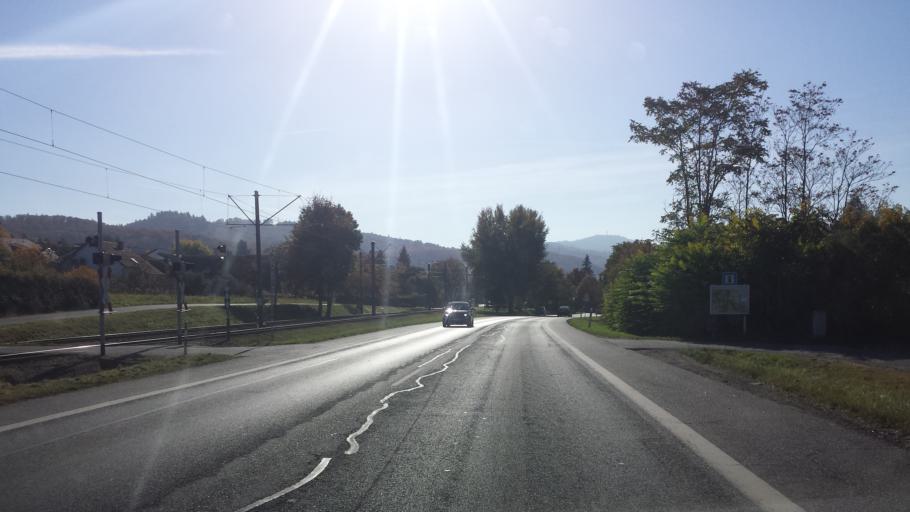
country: DE
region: Hesse
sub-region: Regierungsbezirk Darmstadt
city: Seeheim-Jugenheim
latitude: 49.7775
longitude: 8.6481
